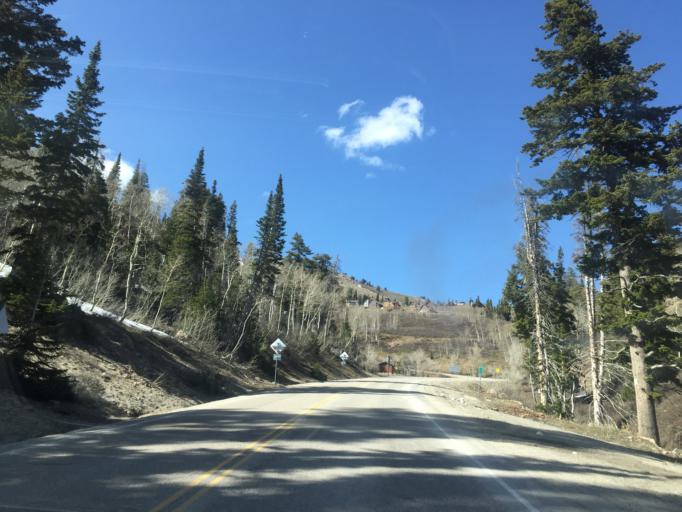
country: US
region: Utah
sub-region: Weber County
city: Wolf Creek
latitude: 41.3751
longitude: -111.7831
